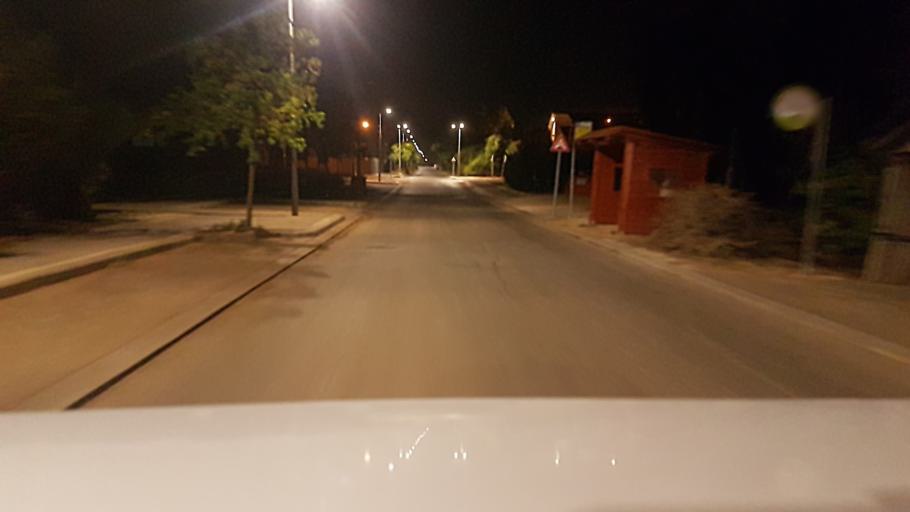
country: IL
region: Central District
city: Nehalim
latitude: 32.0770
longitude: 34.9233
